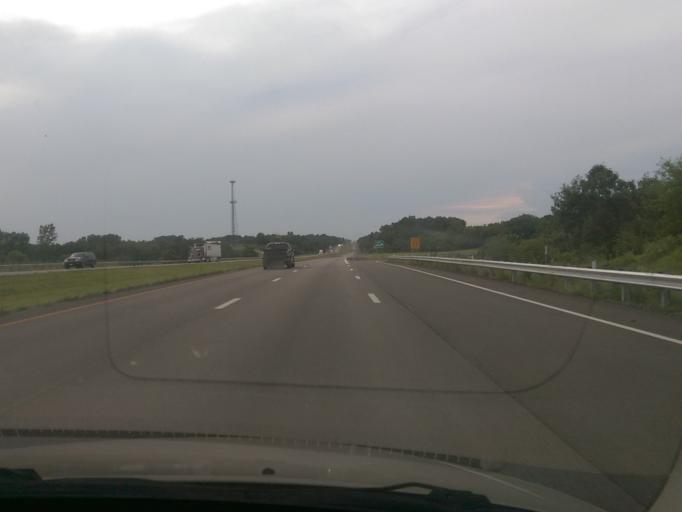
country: US
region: Missouri
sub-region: Andrew County
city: Savannah
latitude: 39.9170
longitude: -94.9057
